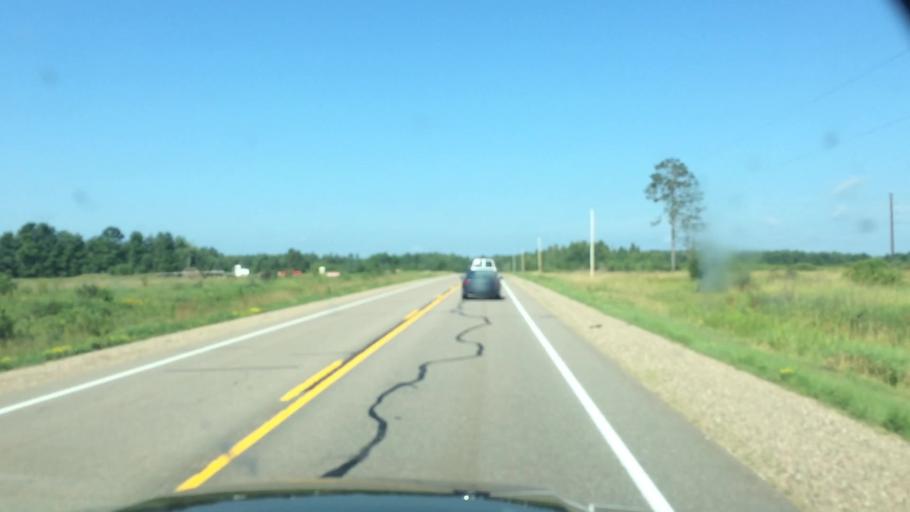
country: US
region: Wisconsin
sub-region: Langlade County
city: Antigo
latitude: 45.1478
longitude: -89.4080
